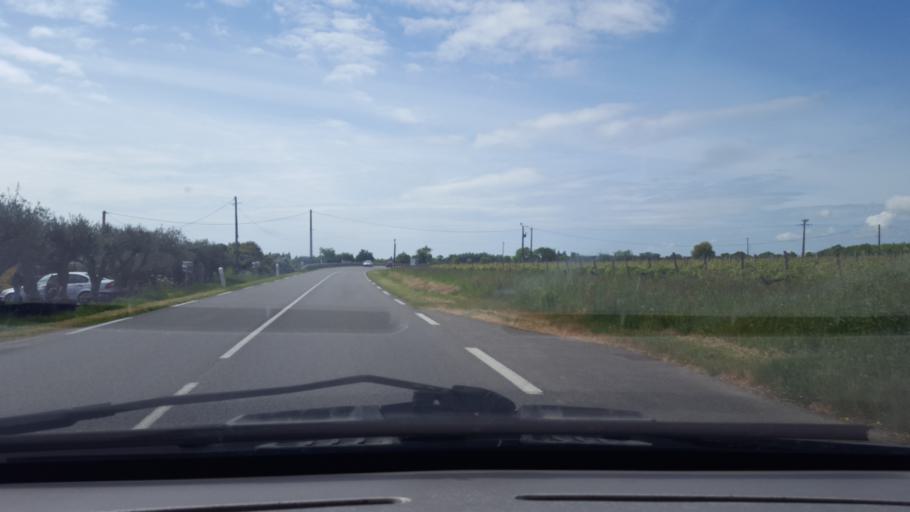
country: FR
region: Pays de la Loire
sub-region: Departement de la Loire-Atlantique
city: Bourgneuf-en-Retz
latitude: 47.0326
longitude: -1.9250
